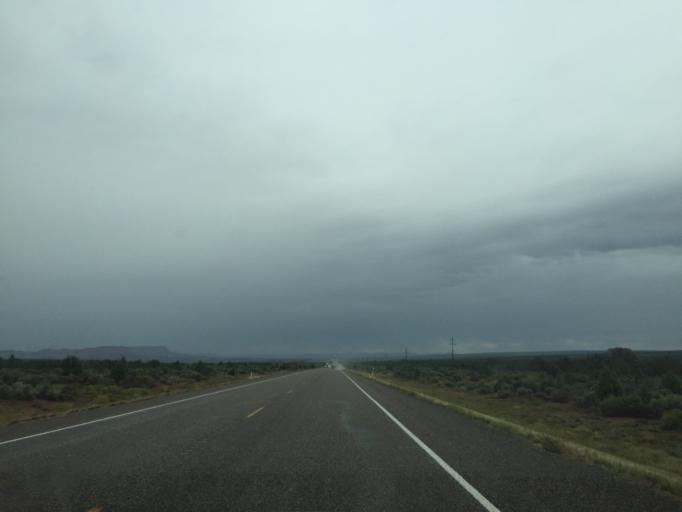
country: US
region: Utah
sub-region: Kane County
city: Kanab
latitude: 37.0811
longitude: -112.1603
